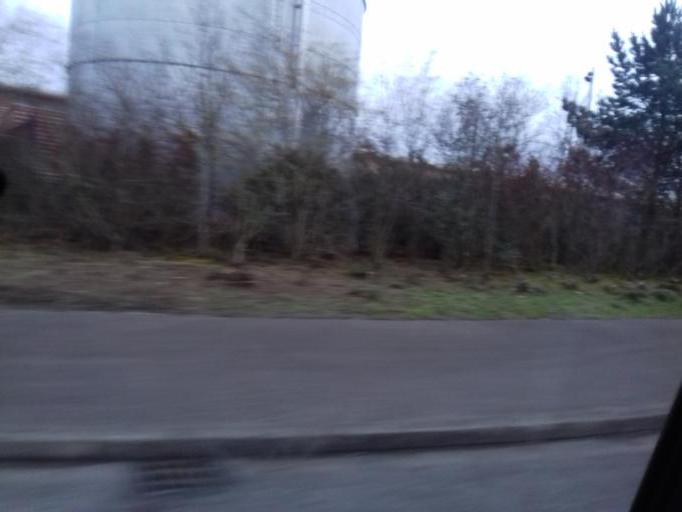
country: GB
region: Northern Ireland
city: Hillsborough
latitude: 54.4904
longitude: -6.0692
